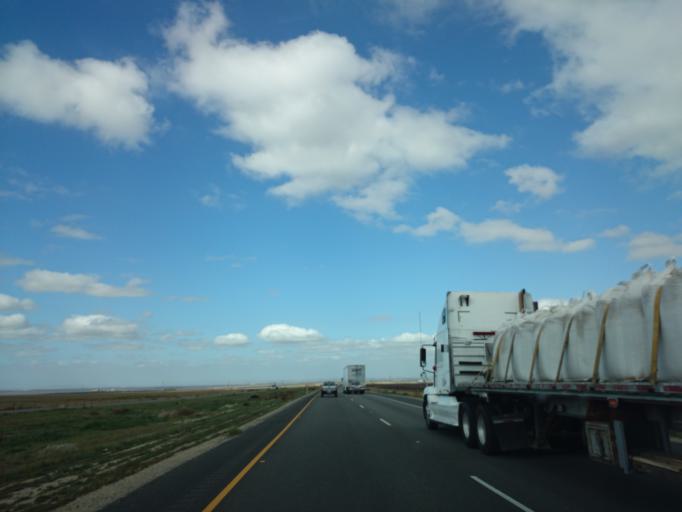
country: US
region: California
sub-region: Kern County
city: Frazier Park
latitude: 35.0284
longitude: -118.9675
